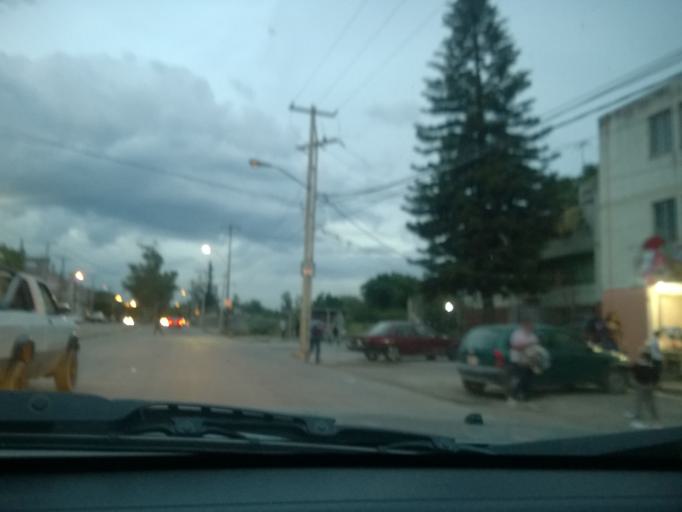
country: MX
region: Guanajuato
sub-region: Leon
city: Medina
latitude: 21.1305
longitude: -101.6410
